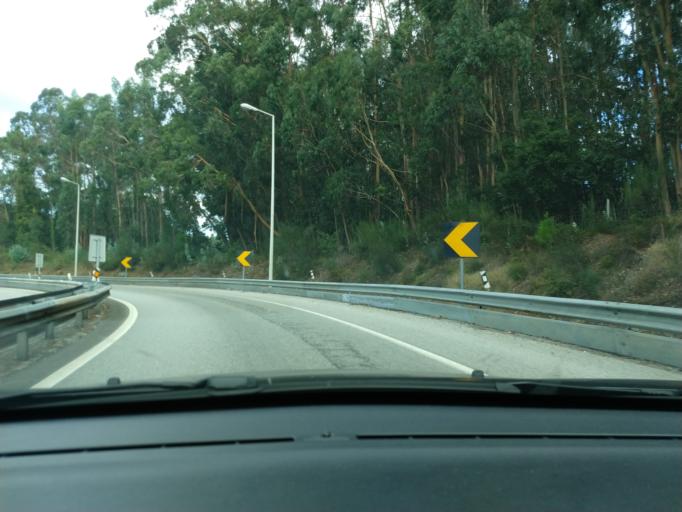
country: PT
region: Aveiro
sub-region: Albergaria-A-Velha
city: Albergaria-a-Velha
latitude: 40.6927
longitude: -8.5207
